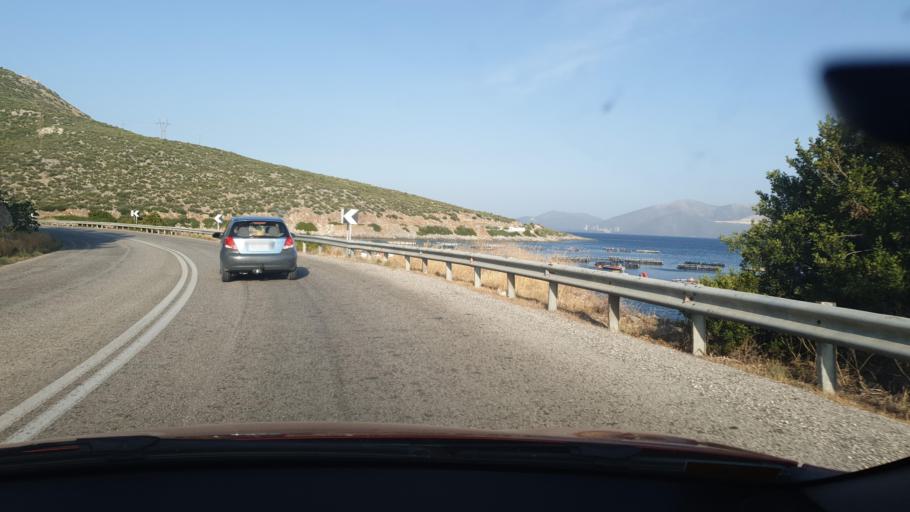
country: GR
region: Central Greece
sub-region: Nomos Evvoias
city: Amarynthos
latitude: 38.3877
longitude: 23.9540
